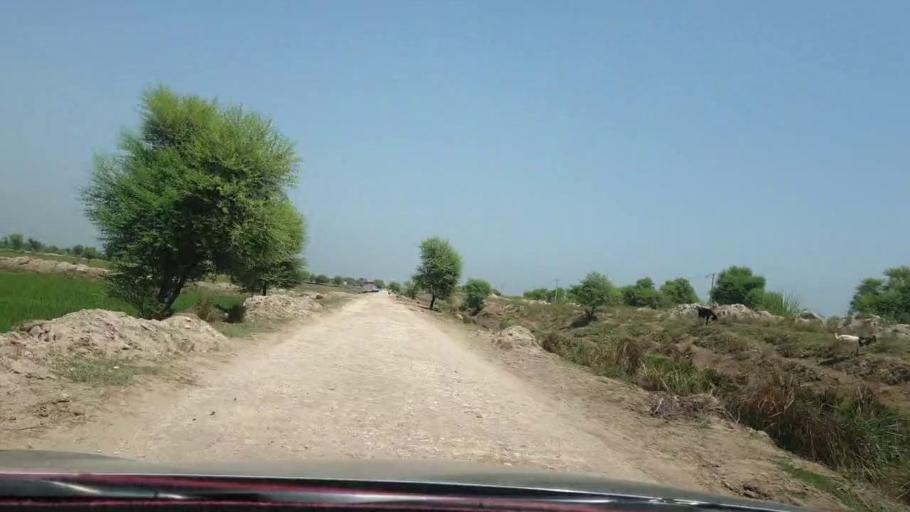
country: PK
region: Sindh
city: Warah
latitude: 27.5087
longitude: 67.7948
